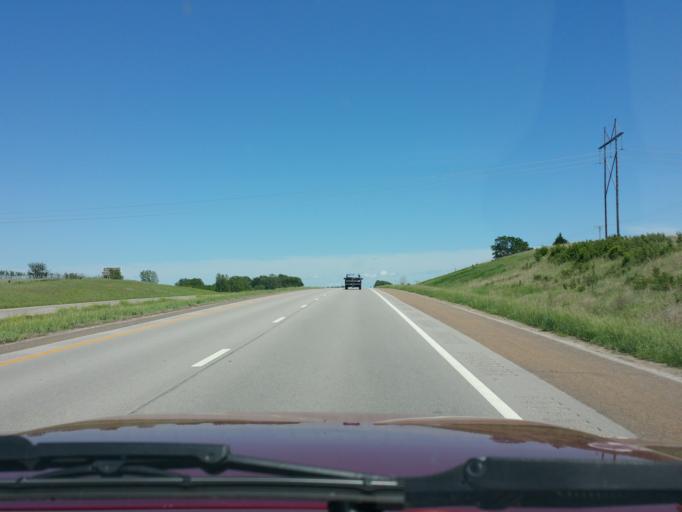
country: US
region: Kansas
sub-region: Pottawatomie County
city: Wamego
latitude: 39.2101
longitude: -96.3824
